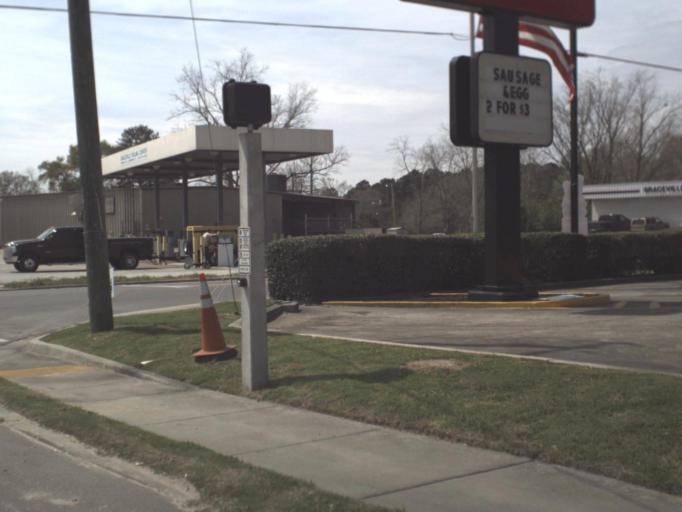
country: US
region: Florida
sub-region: Jackson County
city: Graceville
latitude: 30.9628
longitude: -85.5167
